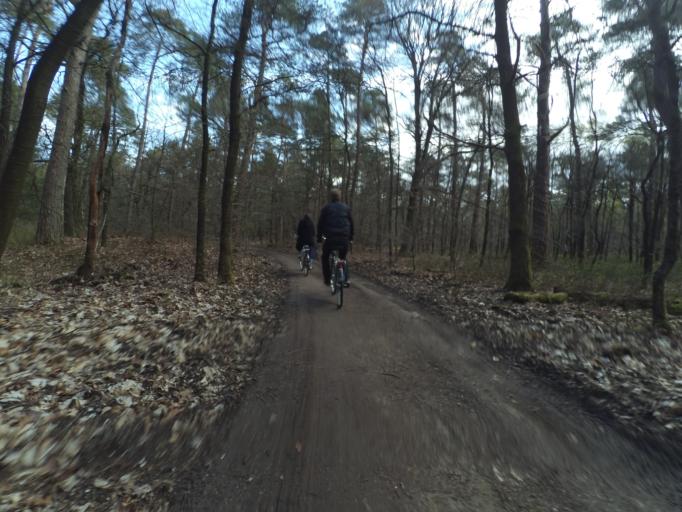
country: NL
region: Gelderland
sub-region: Gemeente Nunspeet
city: Nunspeet
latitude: 52.3464
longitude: 5.8755
